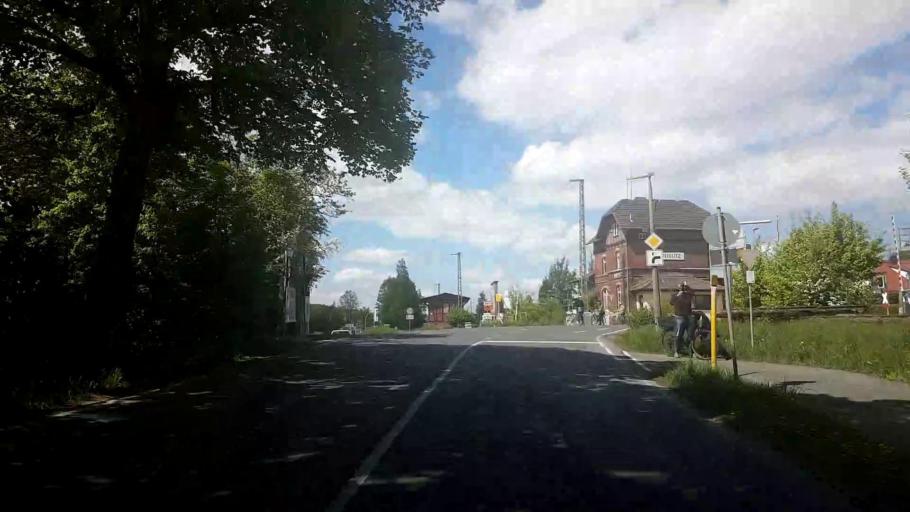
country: DE
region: Bavaria
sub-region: Upper Franconia
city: Niederfullbach
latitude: 50.2264
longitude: 10.9824
